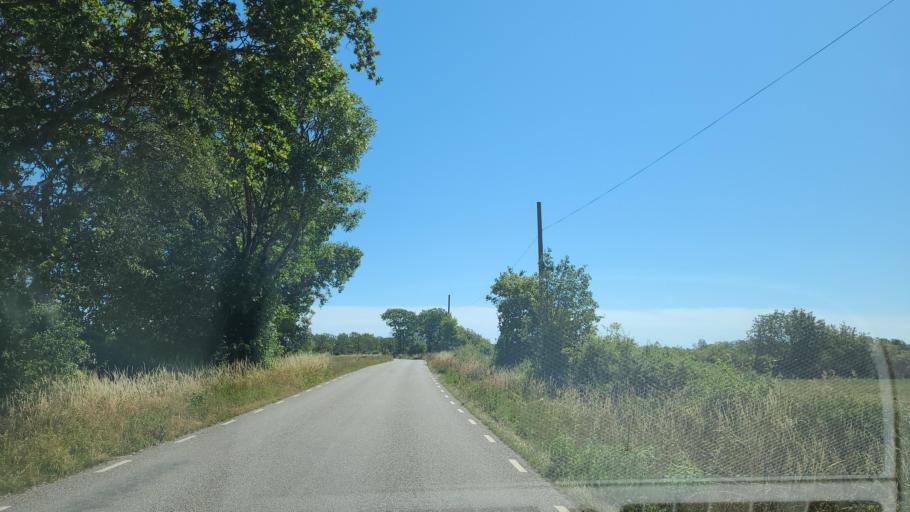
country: SE
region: Kalmar
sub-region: Borgholms Kommun
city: Borgholm
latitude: 56.7680
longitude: 16.5899
